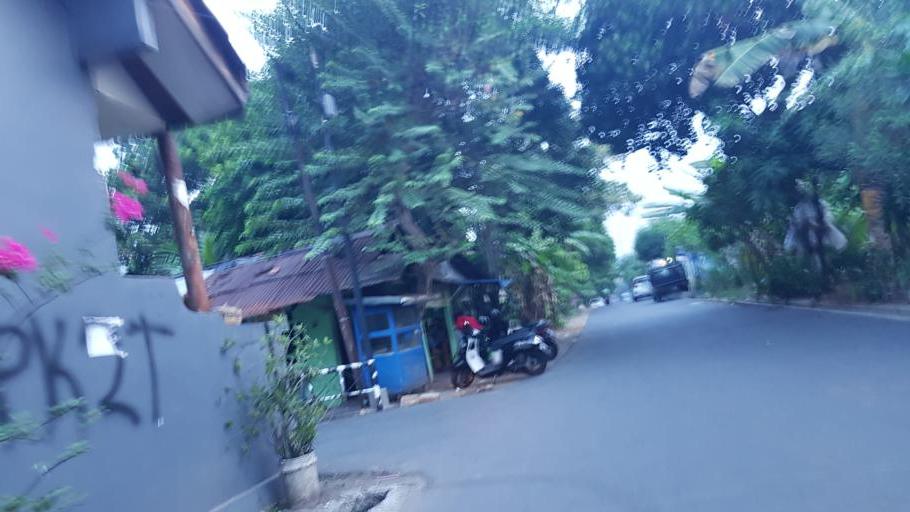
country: ID
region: West Java
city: Pamulang
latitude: -6.3116
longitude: 106.7819
